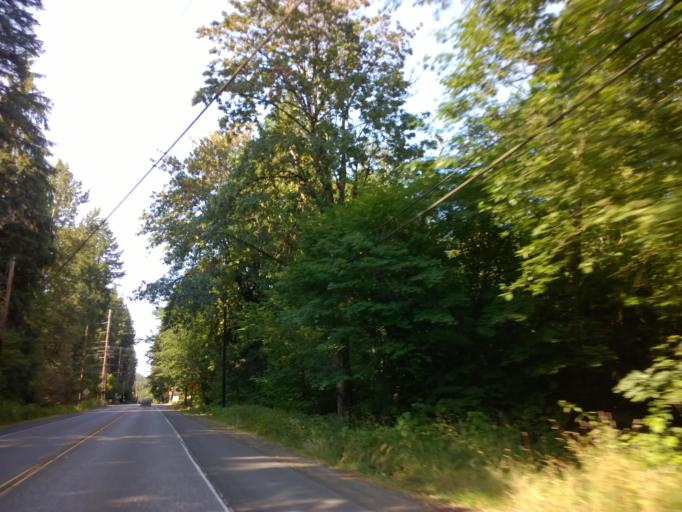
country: US
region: Washington
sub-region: King County
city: Cottage Lake
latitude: 47.7327
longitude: -122.0819
